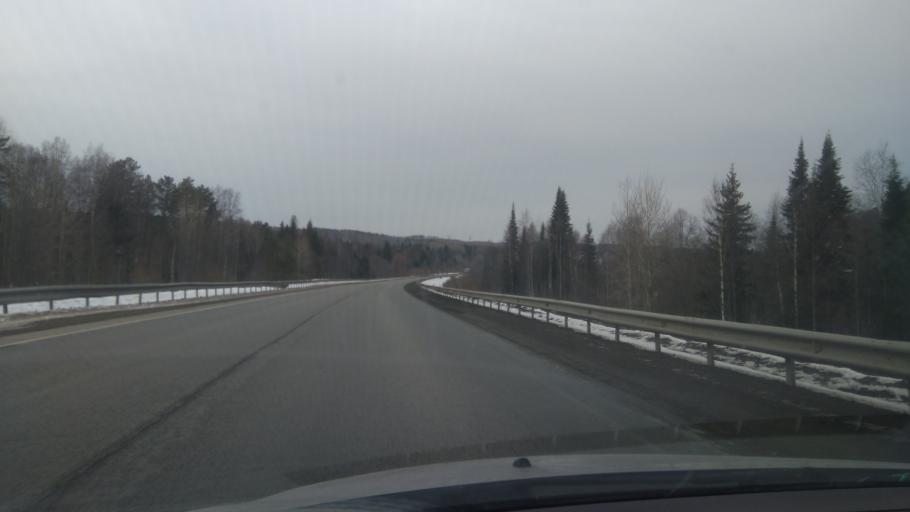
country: RU
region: Sverdlovsk
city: Arti
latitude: 56.7831
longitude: 58.4237
